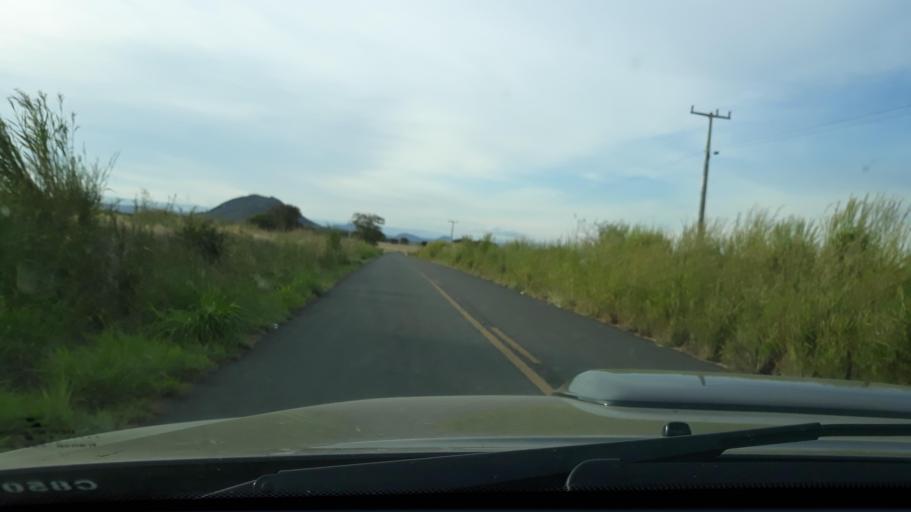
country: BR
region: Bahia
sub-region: Guanambi
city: Guanambi
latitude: -14.1546
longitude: -42.8201
